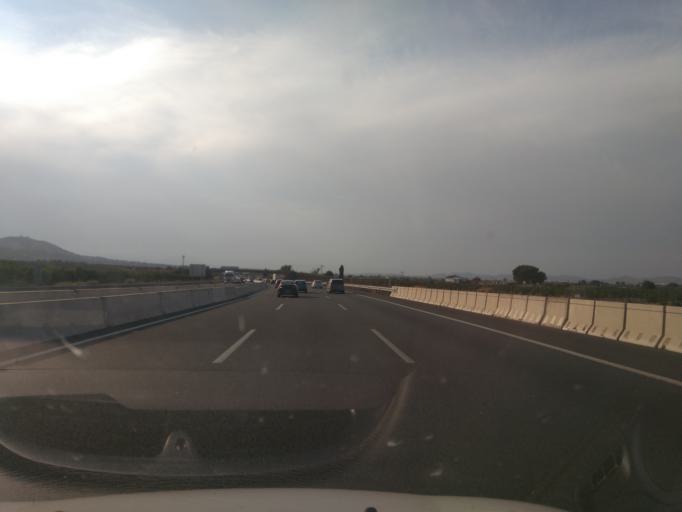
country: ES
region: Valencia
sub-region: Provincia de Valencia
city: Torrent
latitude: 39.4211
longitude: -0.5147
